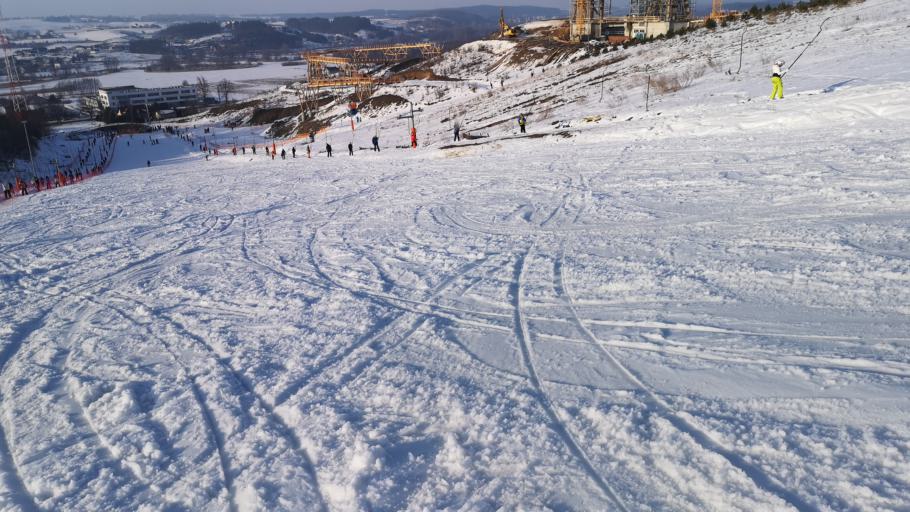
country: PL
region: Warmian-Masurian Voivodeship
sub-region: Powiat nowomiejski
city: Kurzetnik
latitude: 53.3977
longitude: 19.5884
